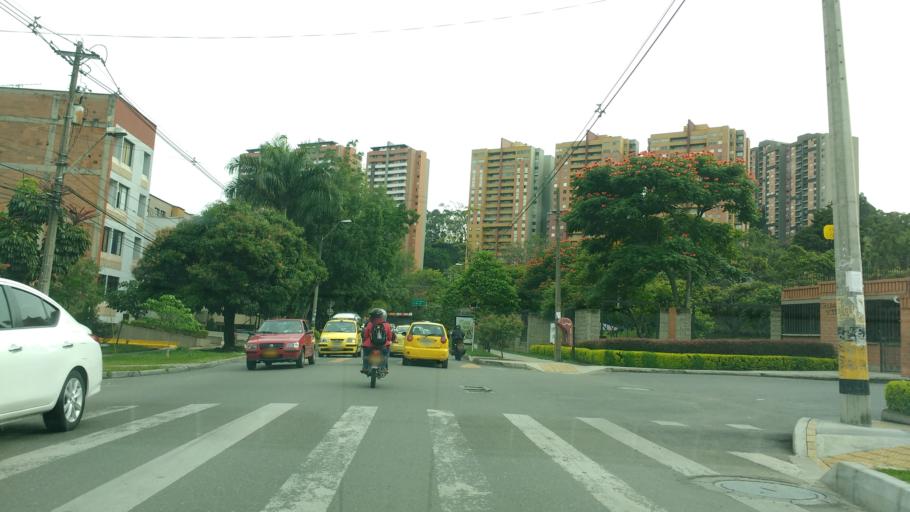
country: CO
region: Antioquia
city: Medellin
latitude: 6.2404
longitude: -75.6081
